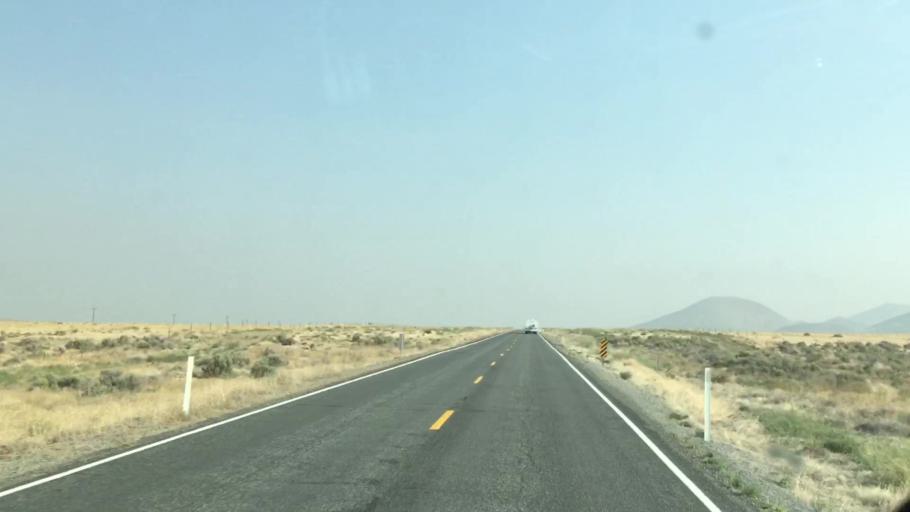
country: US
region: Nevada
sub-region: Lyon County
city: Fernley
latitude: 40.4792
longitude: -119.3345
